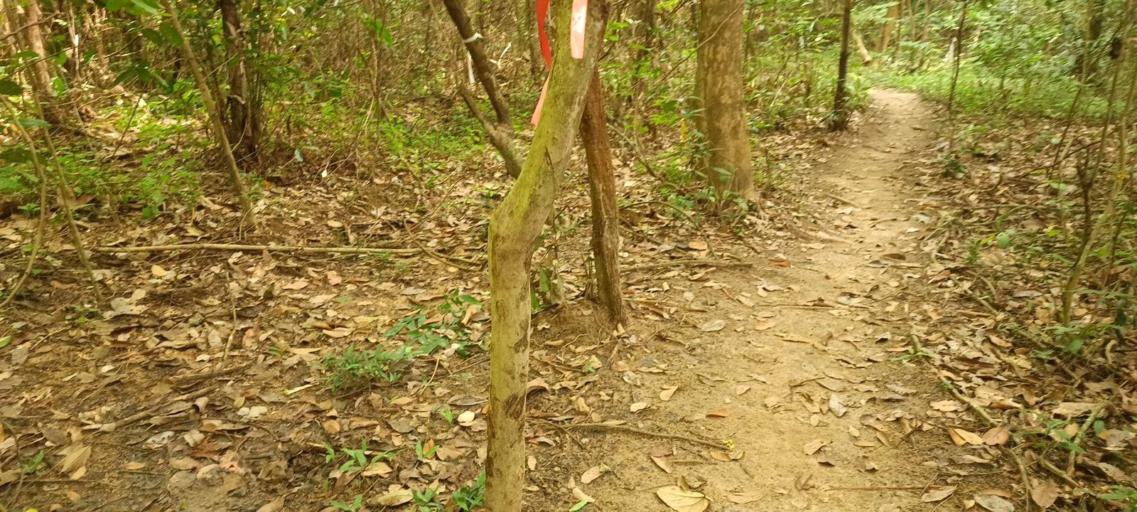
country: MY
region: Penang
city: George Town
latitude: 5.3951
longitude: 100.2931
